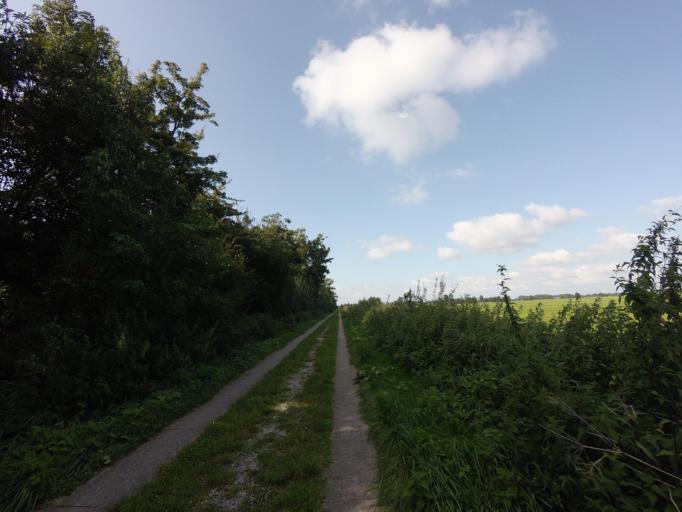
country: NL
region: Flevoland
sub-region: Gemeente Noordoostpolder
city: Ens
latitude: 52.6550
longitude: 5.7749
